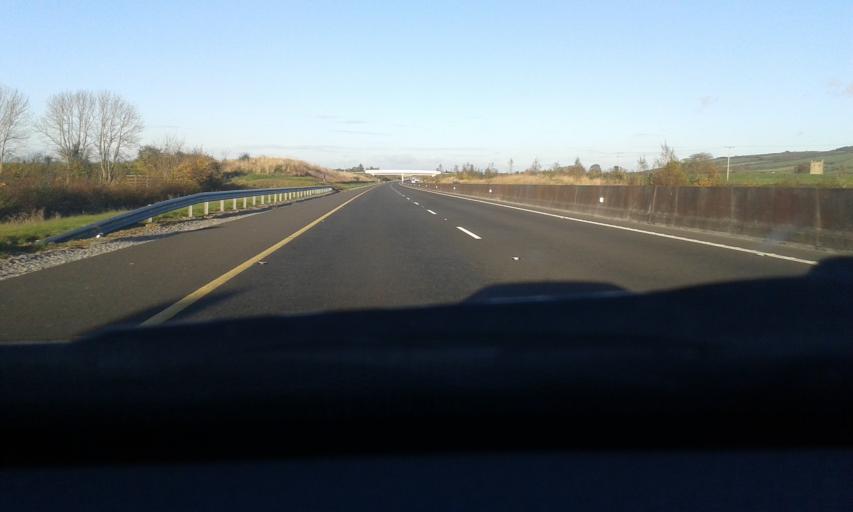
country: IE
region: Leinster
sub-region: Laois
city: Rathdowney
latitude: 52.7853
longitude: -7.5280
